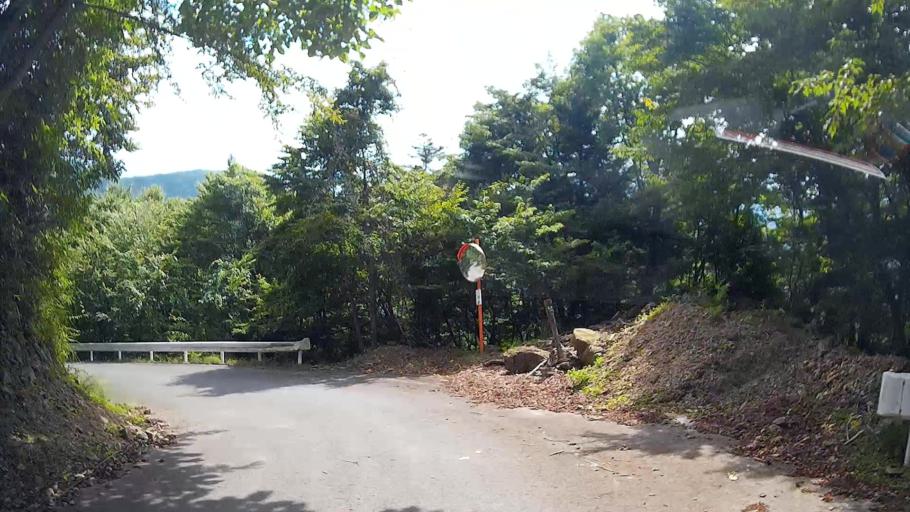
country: JP
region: Saitama
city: Chichibu
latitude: 35.8936
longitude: 139.1075
